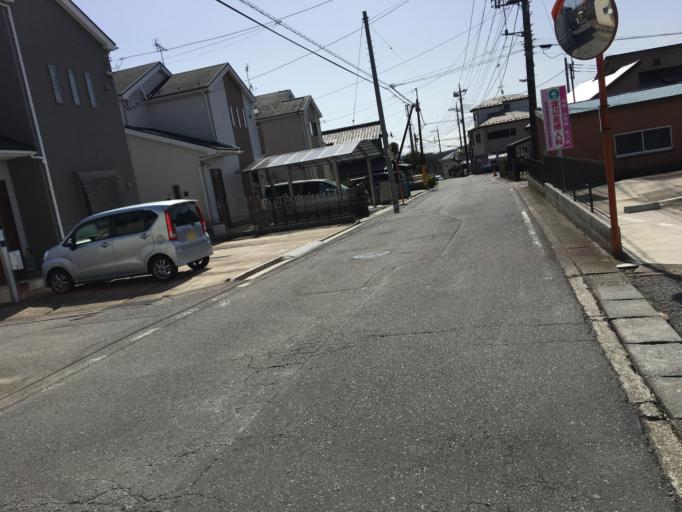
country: JP
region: Saitama
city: Ogawa
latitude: 36.0385
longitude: 139.3292
